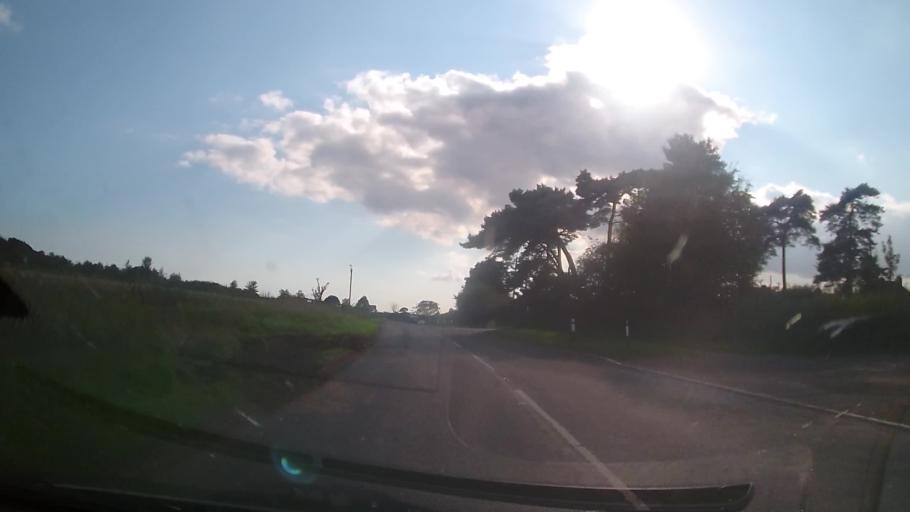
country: GB
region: England
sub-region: Kent
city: Hythe
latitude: 51.0957
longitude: 1.0622
